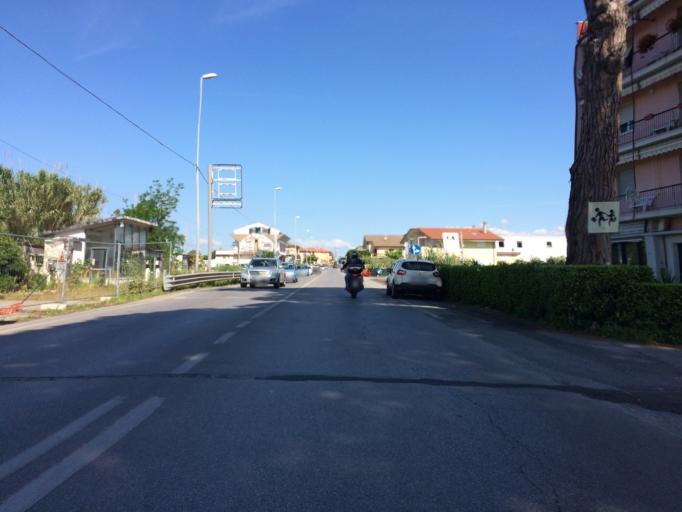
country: IT
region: Liguria
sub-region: Provincia di La Spezia
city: Casano-Dogana-Isola
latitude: 44.0641
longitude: 10.0352
